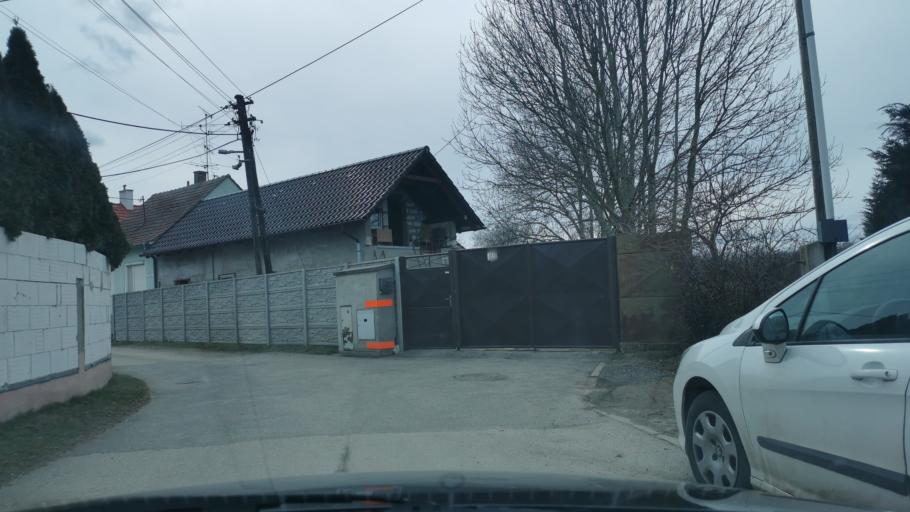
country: CZ
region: South Moravian
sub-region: Okres Breclav
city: Lanzhot
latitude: 48.6907
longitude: 17.0043
